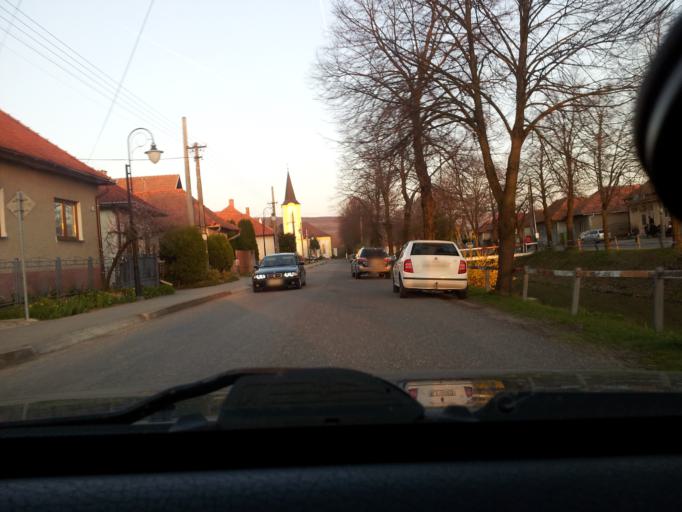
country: SK
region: Nitriansky
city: Tlmace
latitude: 48.3197
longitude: 18.5221
